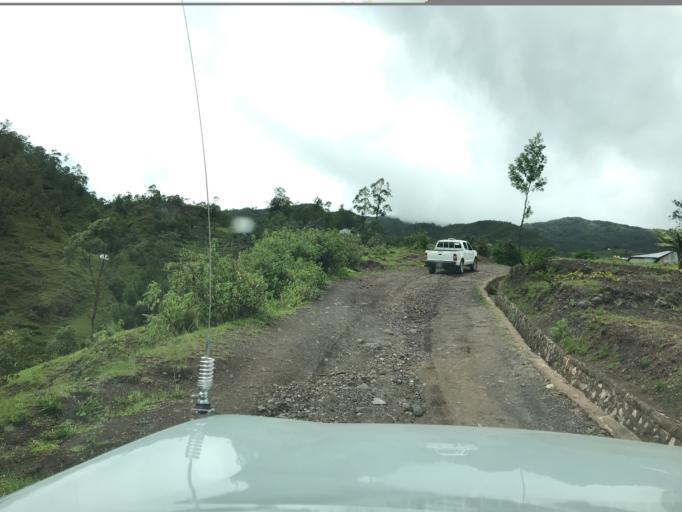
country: TL
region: Aileu
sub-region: Aileu Villa
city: Aileu
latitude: -8.8640
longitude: 125.5575
